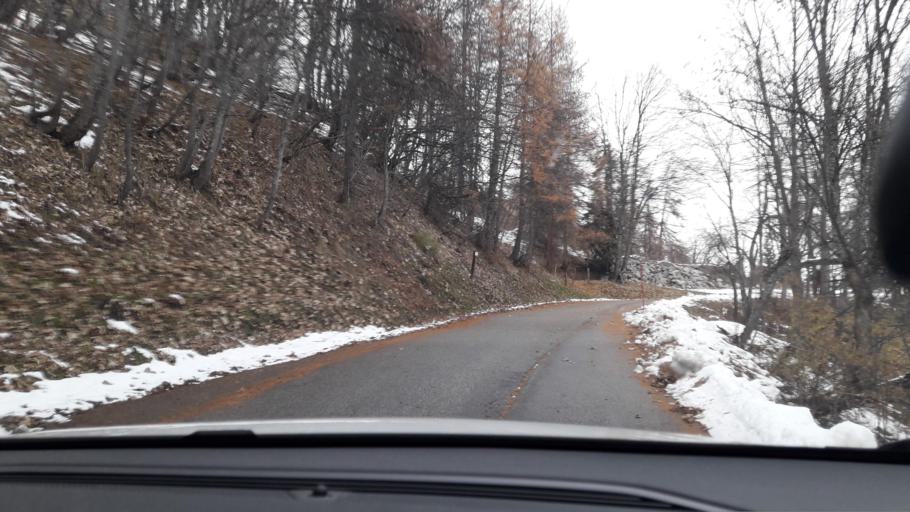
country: FR
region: Rhone-Alpes
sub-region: Departement de la Savoie
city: Valloire
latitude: 45.2004
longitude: 6.4167
